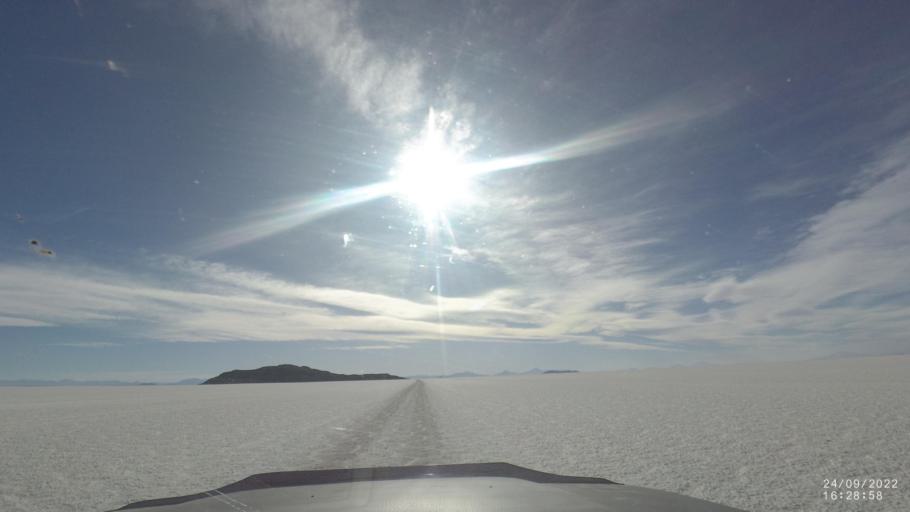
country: BO
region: Potosi
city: Colchani
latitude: -20.2408
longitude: -67.6081
